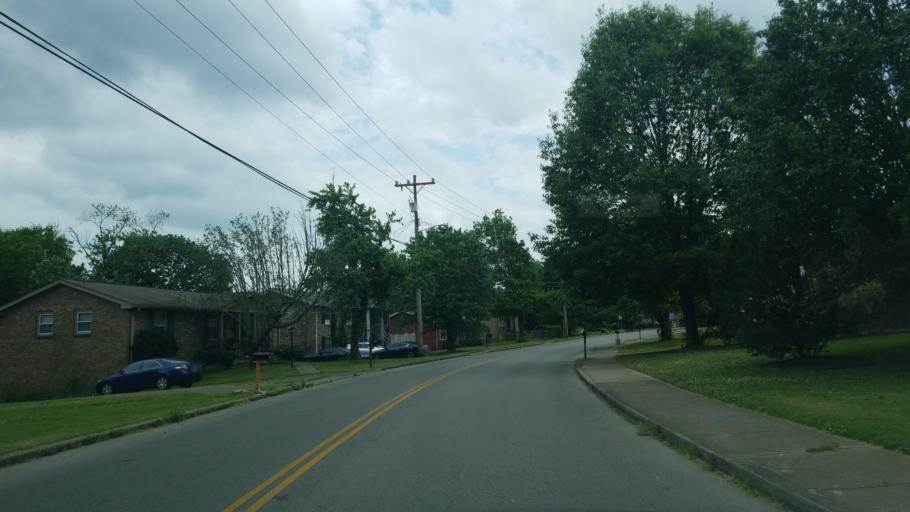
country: US
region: Tennessee
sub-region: Rutherford County
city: La Vergne
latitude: 36.0826
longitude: -86.6233
